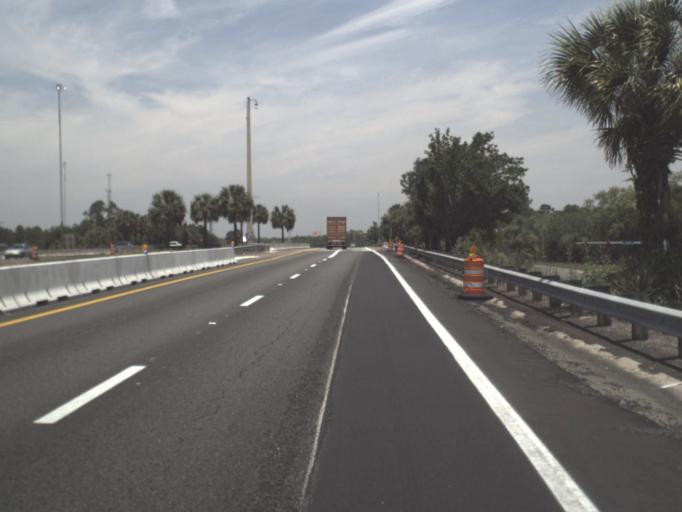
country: US
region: Florida
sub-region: Duval County
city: Jacksonville
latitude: 30.4109
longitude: -81.5646
